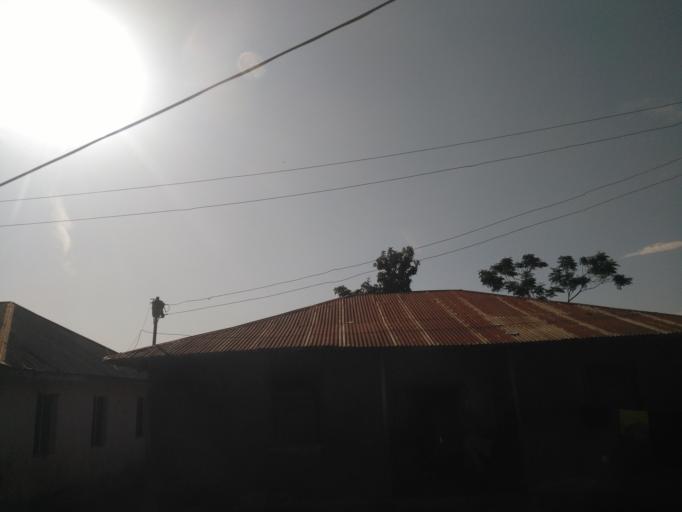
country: TZ
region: Mwanza
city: Mwanza
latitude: -2.5035
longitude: 32.8939
